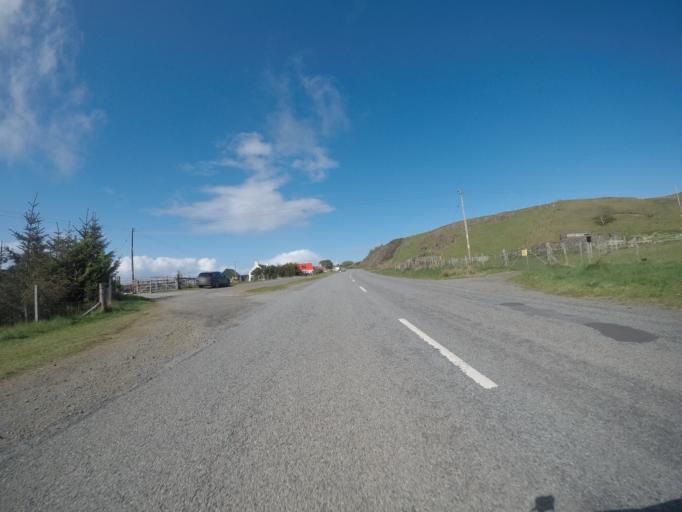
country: GB
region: Scotland
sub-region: Highland
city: Portree
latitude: 57.5846
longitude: -6.1577
